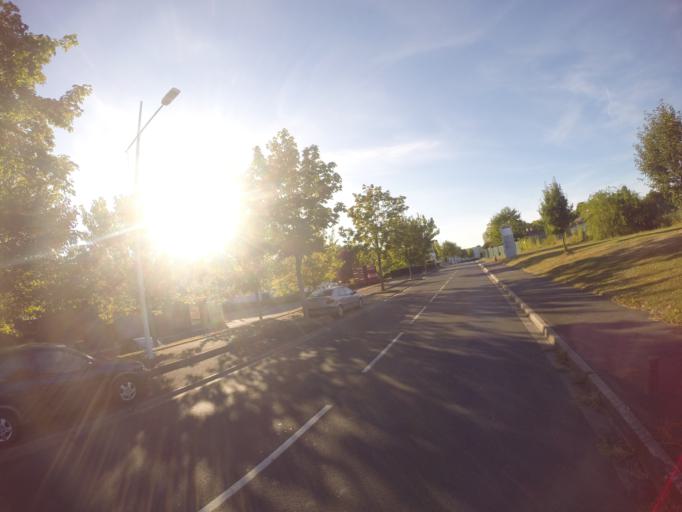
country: FR
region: Centre
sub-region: Departement d'Indre-et-Loire
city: Chanceaux-sur-Choisille
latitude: 47.4300
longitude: 0.7082
